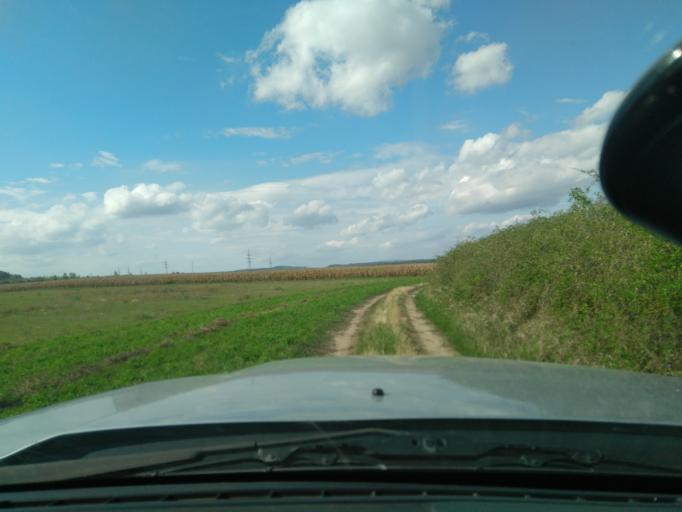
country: HU
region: Fejer
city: Bicske
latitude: 47.4739
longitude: 18.6704
